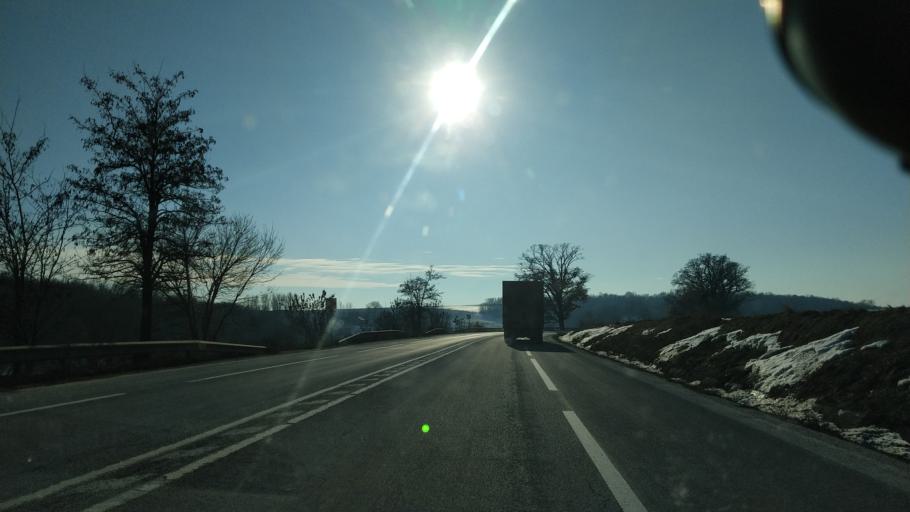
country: RO
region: Iasi
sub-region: Comuna Butea
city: Butea
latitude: 47.1156
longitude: 26.9406
